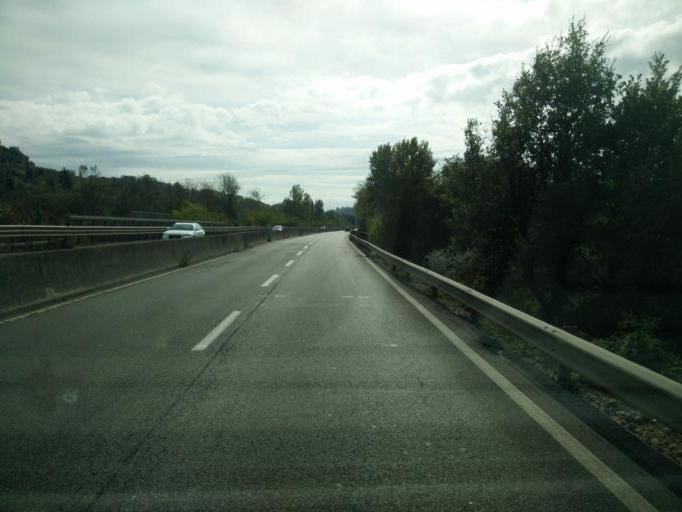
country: IT
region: Tuscany
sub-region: Provincia di Siena
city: Belverde
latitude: 43.3274
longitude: 11.2952
